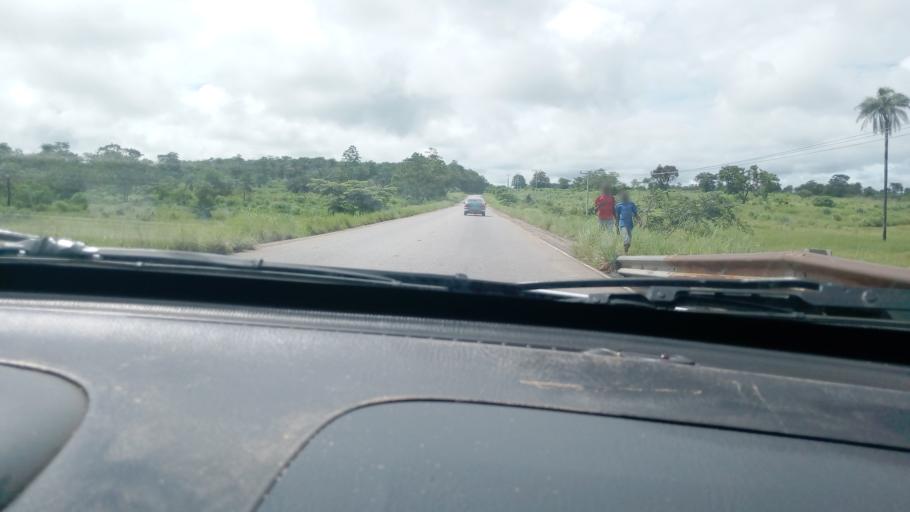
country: SL
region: Northern Province
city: Makeni
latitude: 8.8031
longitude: -12.0349
